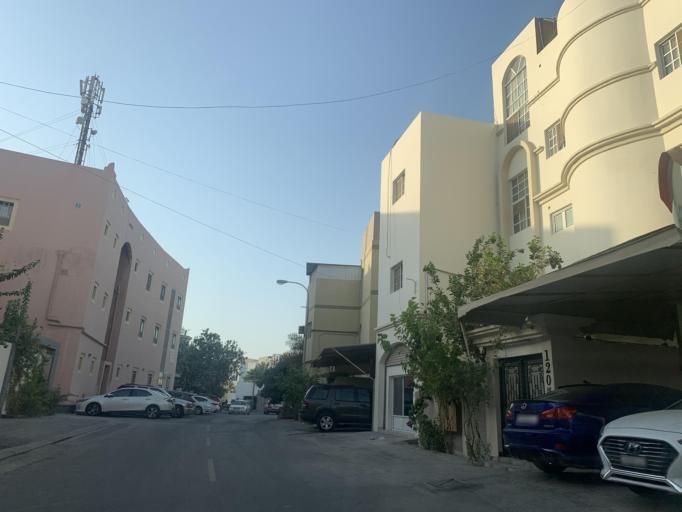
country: BH
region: Muharraq
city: Al Muharraq
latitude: 26.2806
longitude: 50.6369
